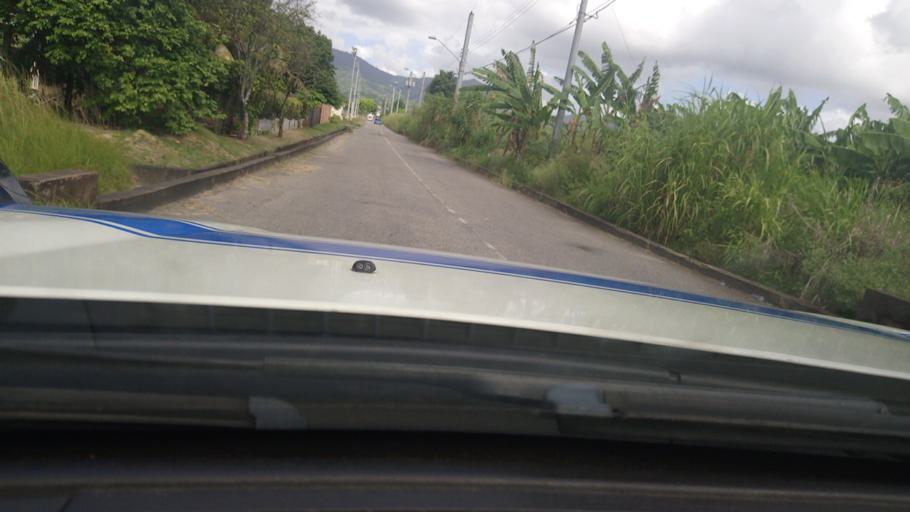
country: TT
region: Borough of Arima
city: Arima
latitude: 10.6207
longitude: -61.3017
